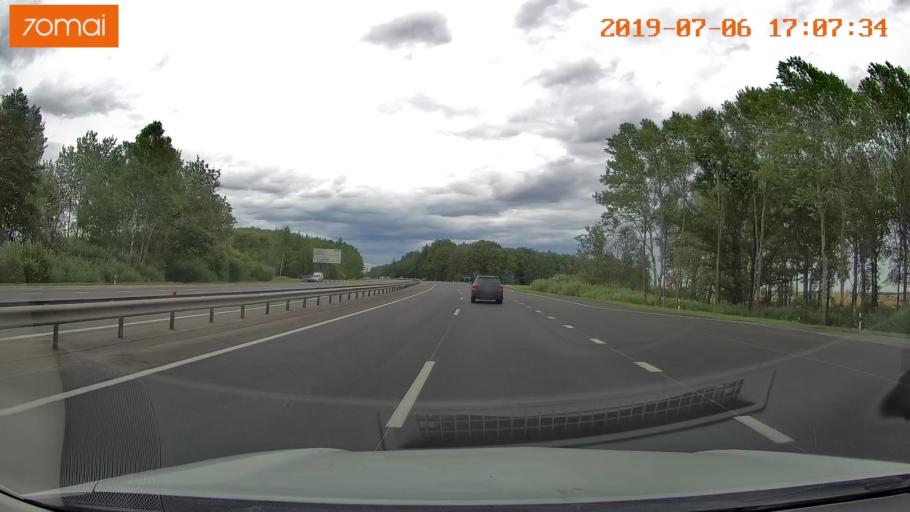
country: BY
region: Minsk
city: Khatsyezhyna
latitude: 53.9072
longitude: 27.3673
